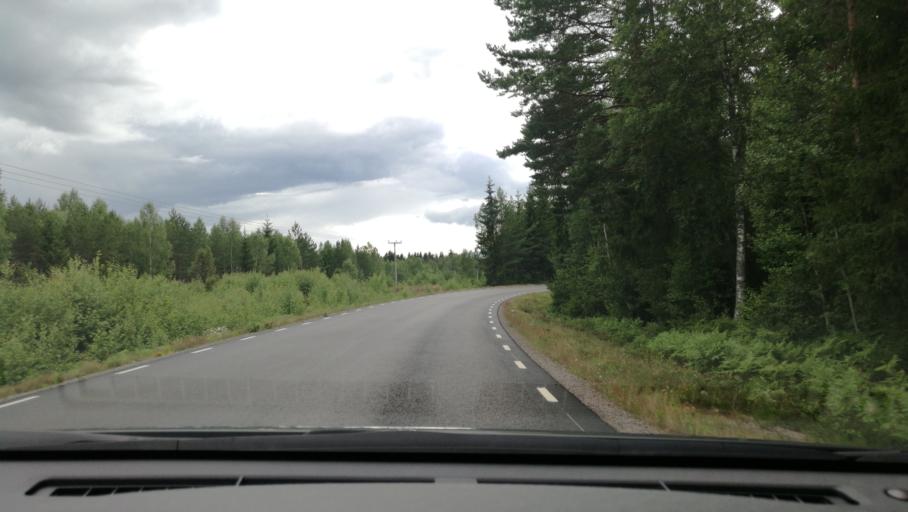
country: SE
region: OEstergoetland
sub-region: Norrkopings Kommun
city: Svartinge
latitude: 58.8177
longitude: 16.0254
